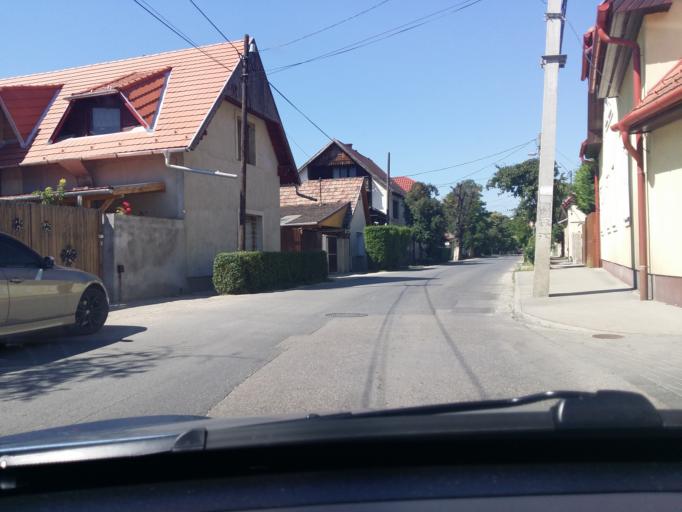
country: HU
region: Pest
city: Nagykovacsi
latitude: 47.6505
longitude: 19.0205
